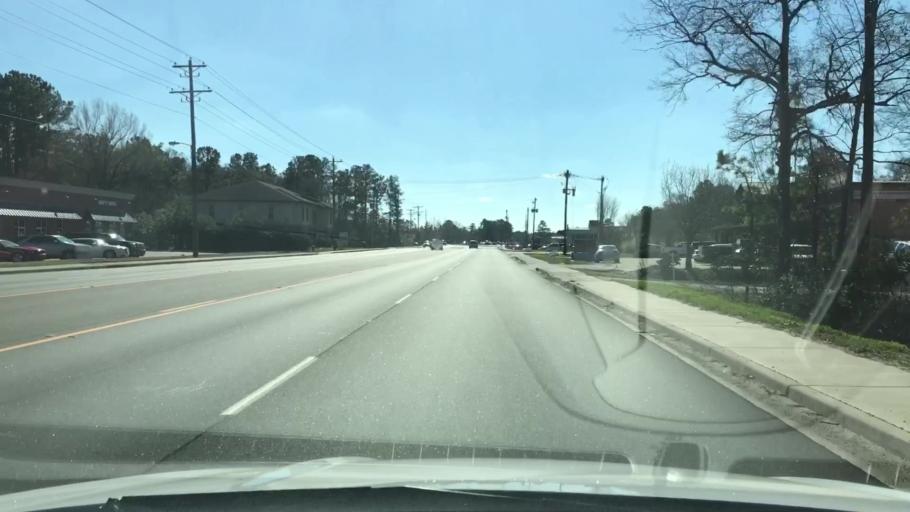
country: US
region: South Carolina
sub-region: Horry County
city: Garden City
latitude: 33.6343
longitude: -79.0337
